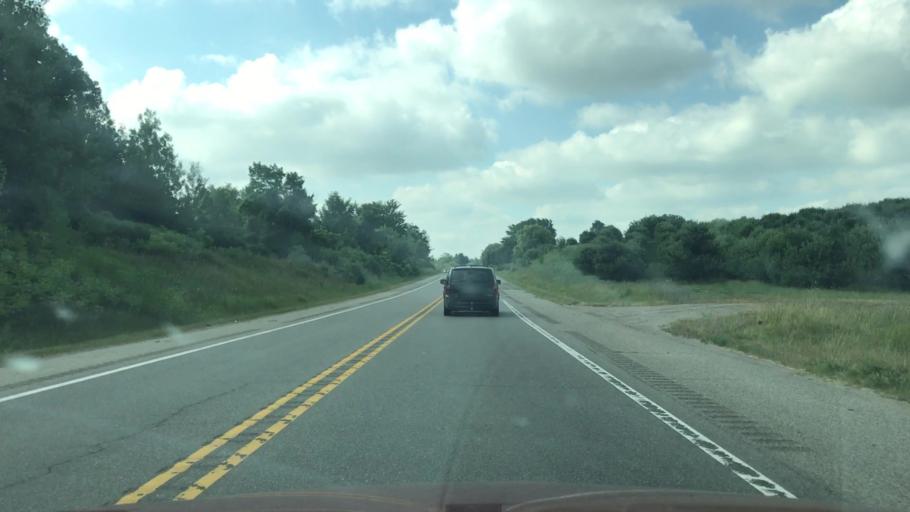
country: US
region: Michigan
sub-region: Kent County
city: Kent City
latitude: 43.2605
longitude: -85.8154
